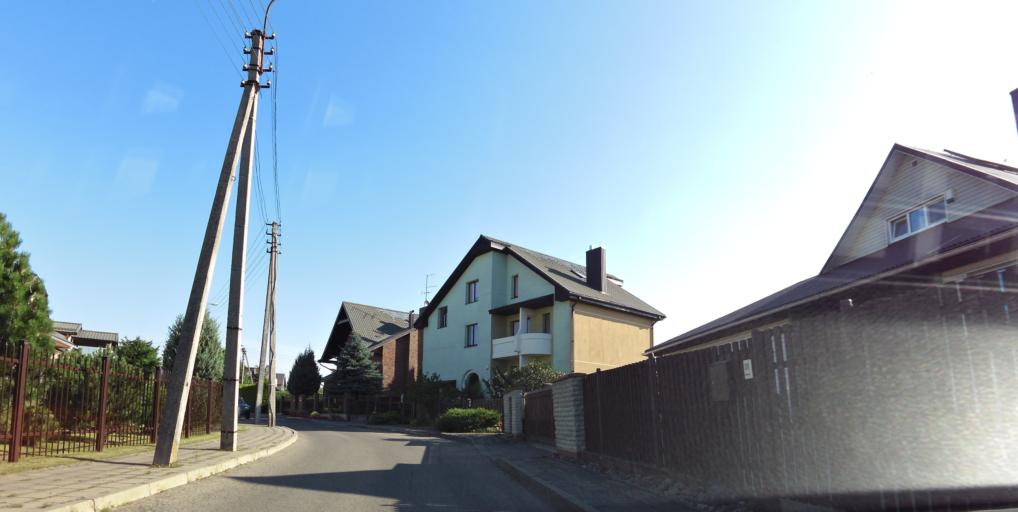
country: LT
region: Vilnius County
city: Pilaite
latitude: 54.7112
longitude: 25.1941
